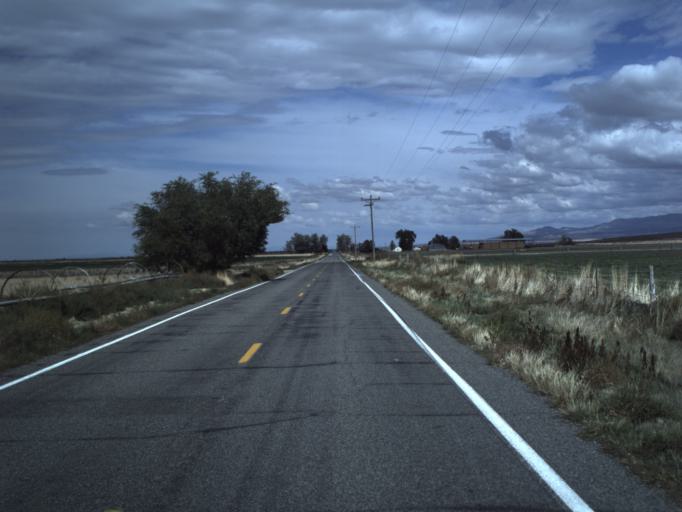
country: US
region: Utah
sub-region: Millard County
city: Fillmore
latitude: 39.0512
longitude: -112.4098
